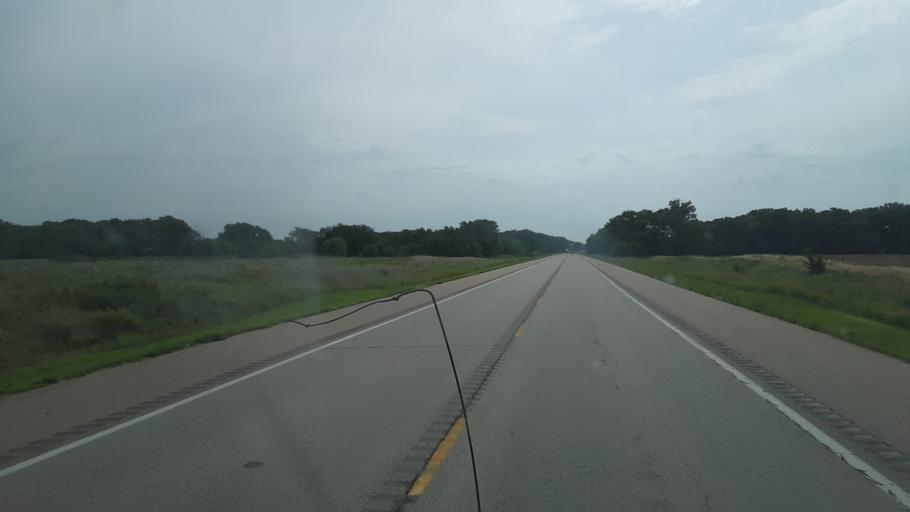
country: US
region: Kansas
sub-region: Stafford County
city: Stafford
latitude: 37.9844
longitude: -98.3787
